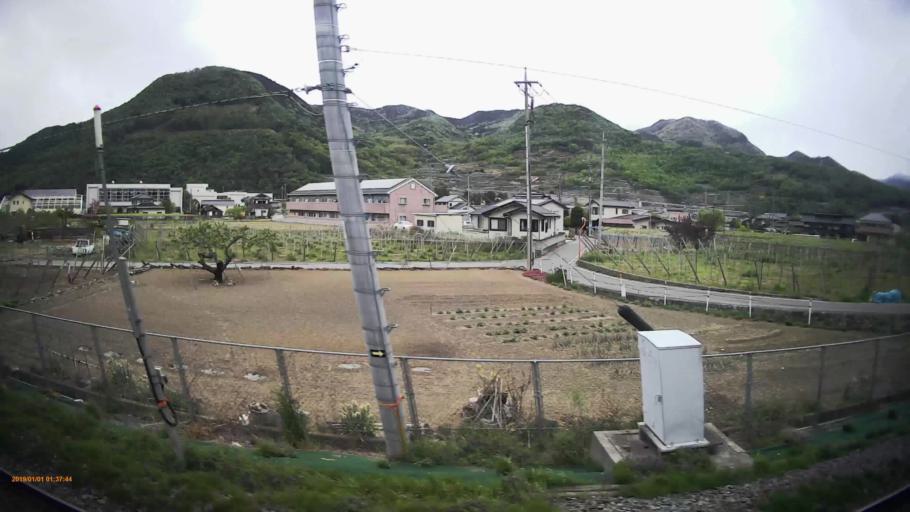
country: JP
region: Yamanashi
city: Isawa
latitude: 35.6632
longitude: 138.6461
